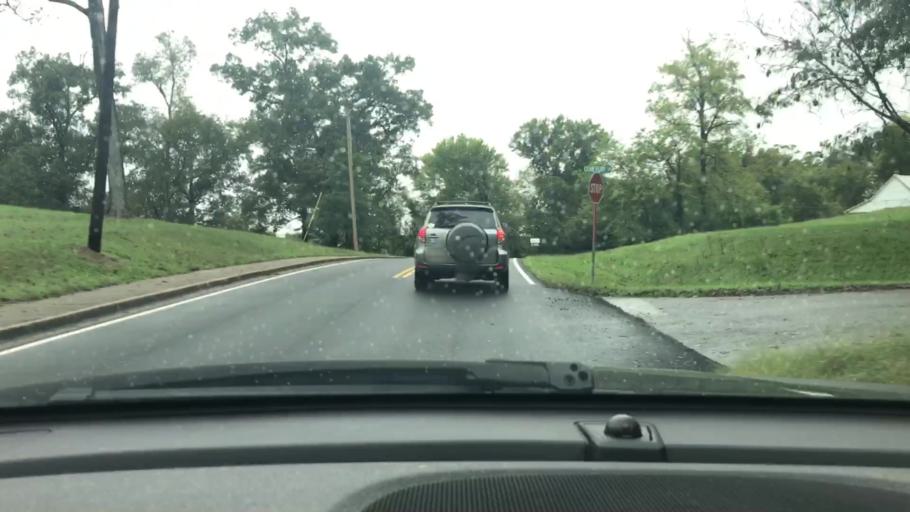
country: US
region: Tennessee
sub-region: Cheatham County
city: Kingston Springs
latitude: 36.0984
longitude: -87.1133
